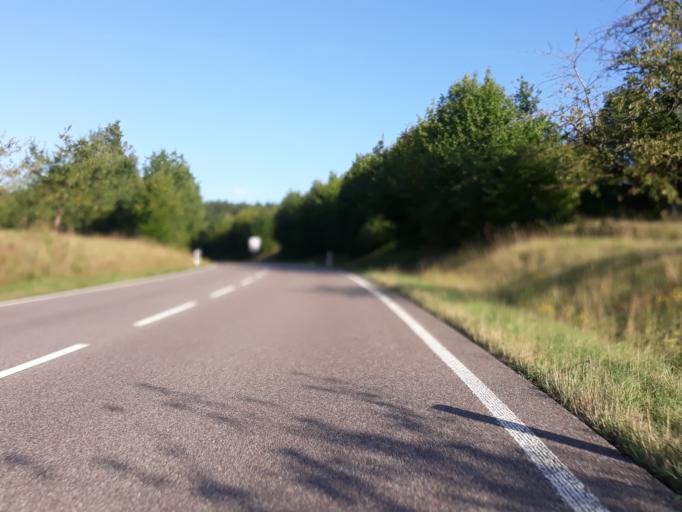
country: DE
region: Baden-Wuerttemberg
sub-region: Regierungsbezirk Stuttgart
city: Nufringen
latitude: 48.6144
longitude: 8.8778
